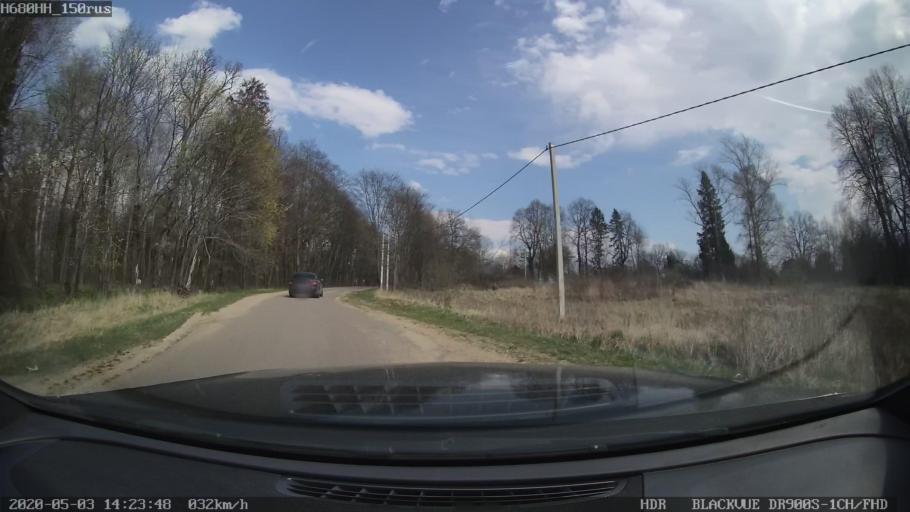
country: RU
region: Moskovskaya
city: Solnechnogorsk
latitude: 56.2518
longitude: 36.9950
